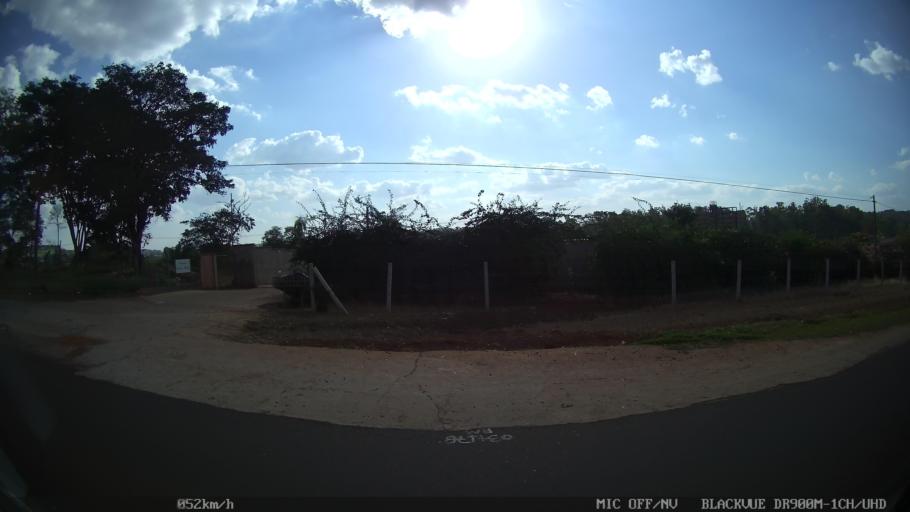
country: BR
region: Sao Paulo
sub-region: Ribeirao Preto
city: Ribeirao Preto
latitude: -21.1785
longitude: -47.8548
